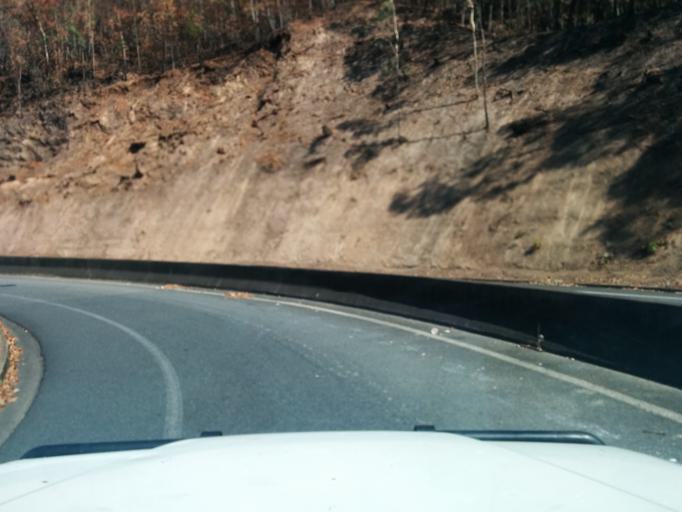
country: AU
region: Queensland
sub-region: Cairns
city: Cairns
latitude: -16.9152
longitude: 145.7279
